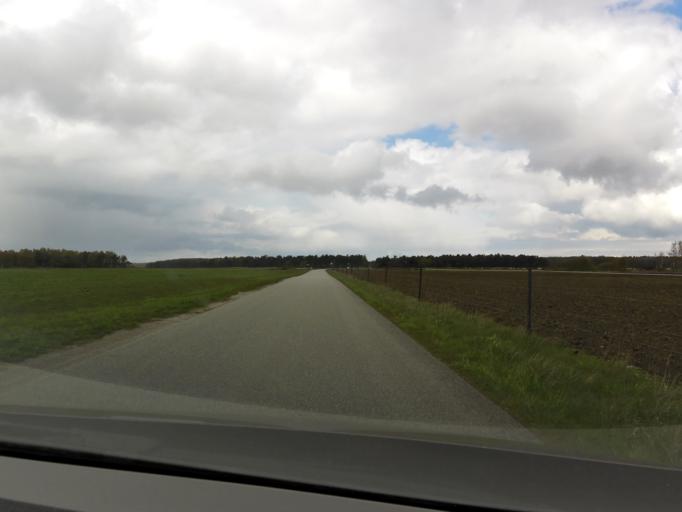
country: DE
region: Mecklenburg-Vorpommern
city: Born
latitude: 54.3877
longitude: 12.5007
